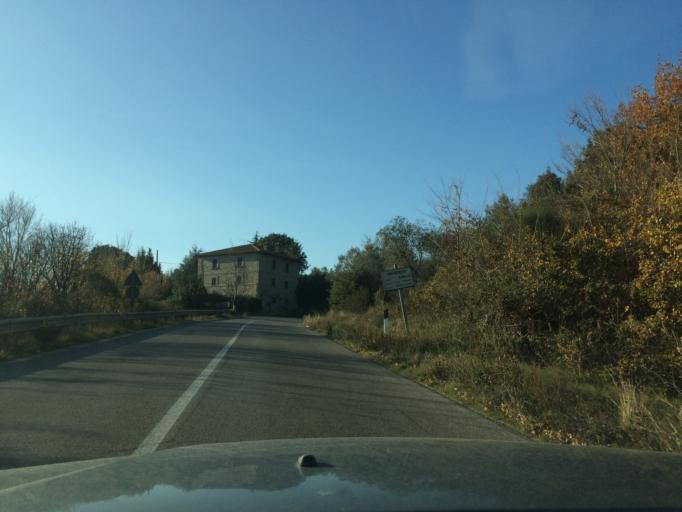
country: IT
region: Umbria
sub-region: Provincia di Terni
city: Fornole
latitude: 42.5394
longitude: 12.4700
